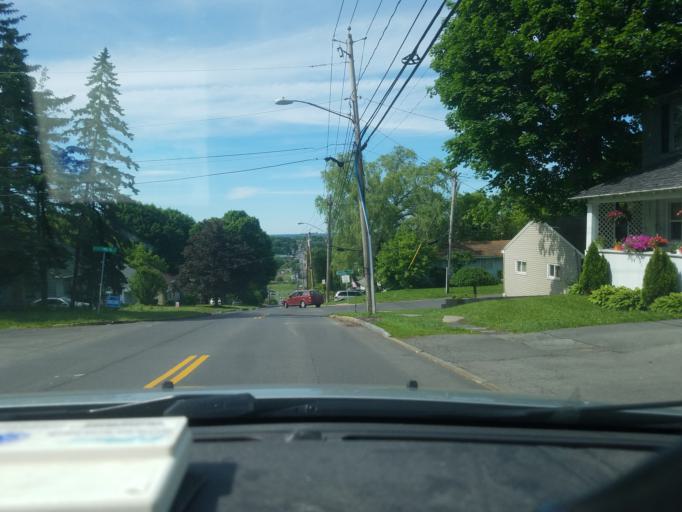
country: US
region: New York
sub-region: Onondaga County
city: East Syracuse
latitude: 43.0502
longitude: -76.1038
